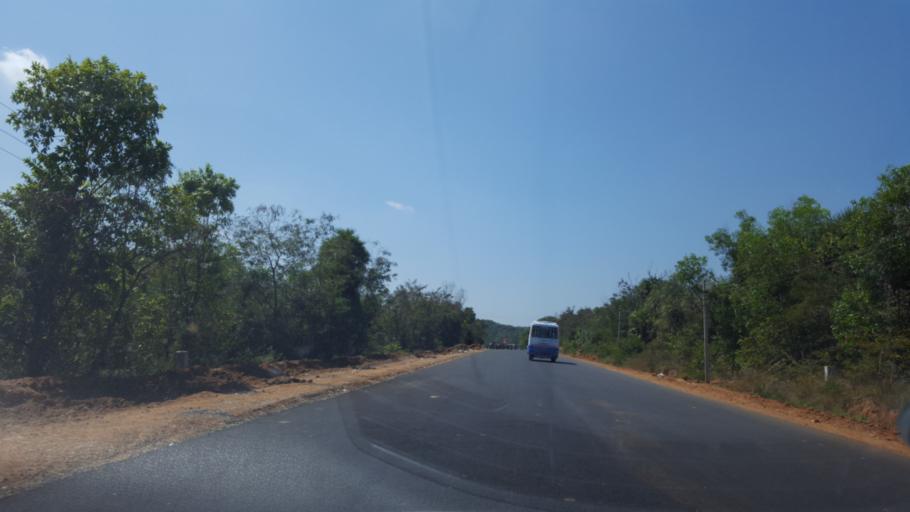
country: IN
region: Tamil Nadu
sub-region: Kancheepuram
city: Karumbakkam
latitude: 12.6238
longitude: 80.0583
